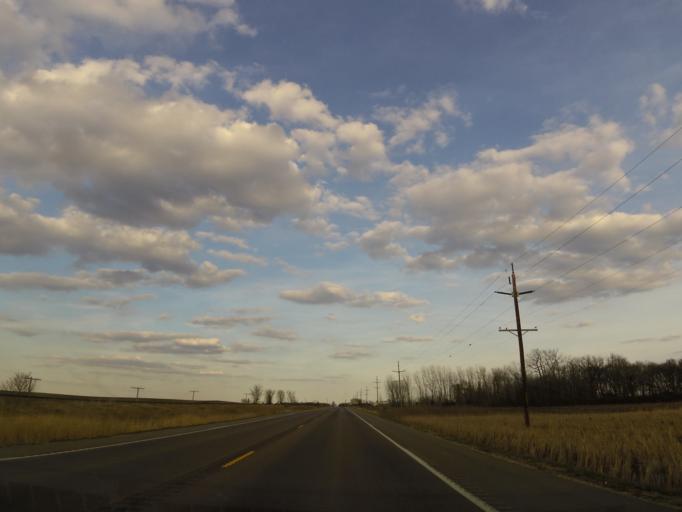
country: US
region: Minnesota
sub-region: Renville County
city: Hector
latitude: 44.7243
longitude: -94.5264
